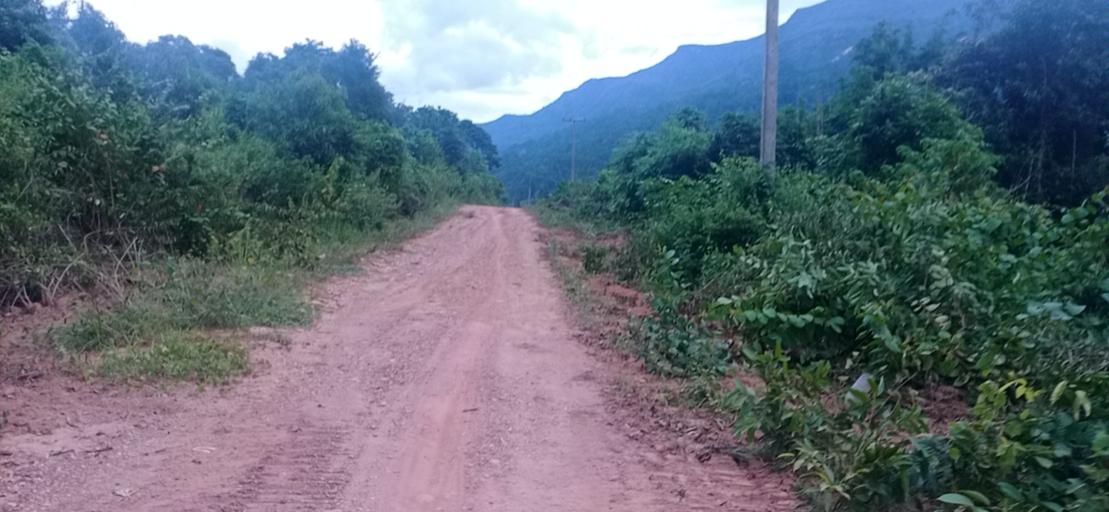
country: TH
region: Changwat Bueng Kan
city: Pak Khat
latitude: 18.5594
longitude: 103.2324
